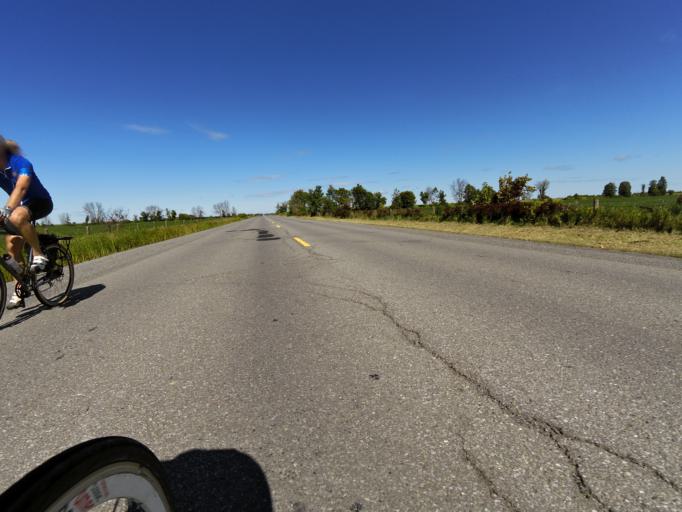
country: CA
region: Ontario
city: Bells Corners
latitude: 45.2102
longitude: -75.8257
